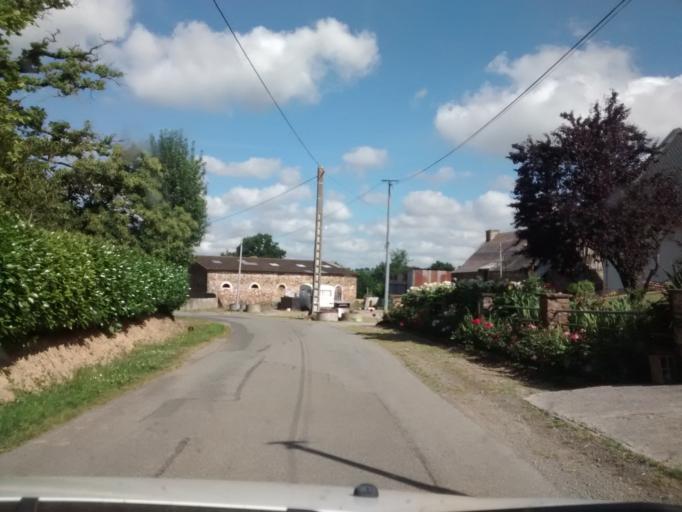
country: FR
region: Brittany
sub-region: Departement d'Ille-et-Vilaine
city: Bain-de-Bretagne
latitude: 47.8325
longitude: -1.7099
